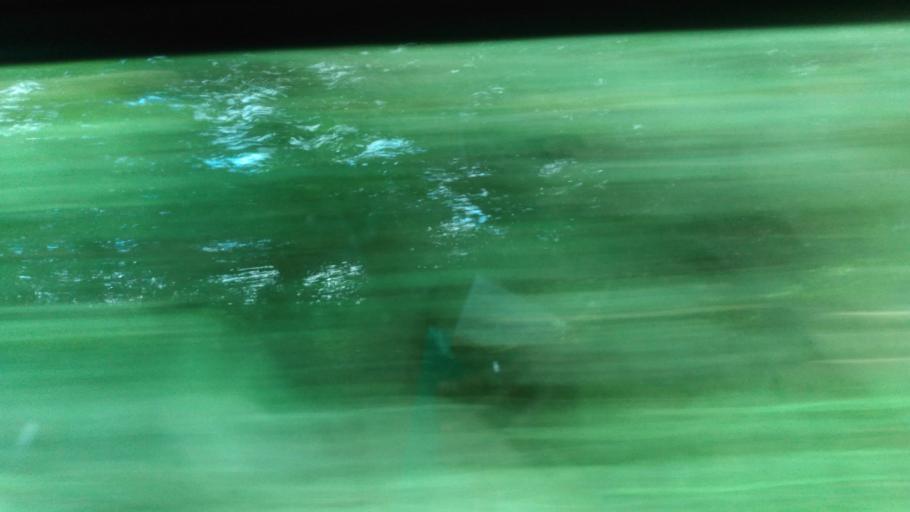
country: BR
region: Pernambuco
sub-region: Quipapa
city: Quipapa
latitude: -8.7876
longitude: -35.9766
